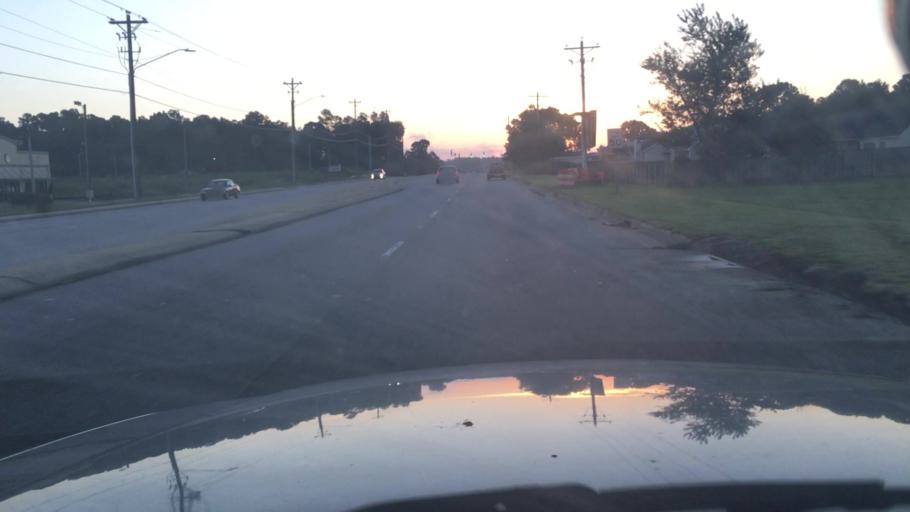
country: US
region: North Carolina
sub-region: Hoke County
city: Rockfish
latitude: 35.0597
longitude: -79.0475
